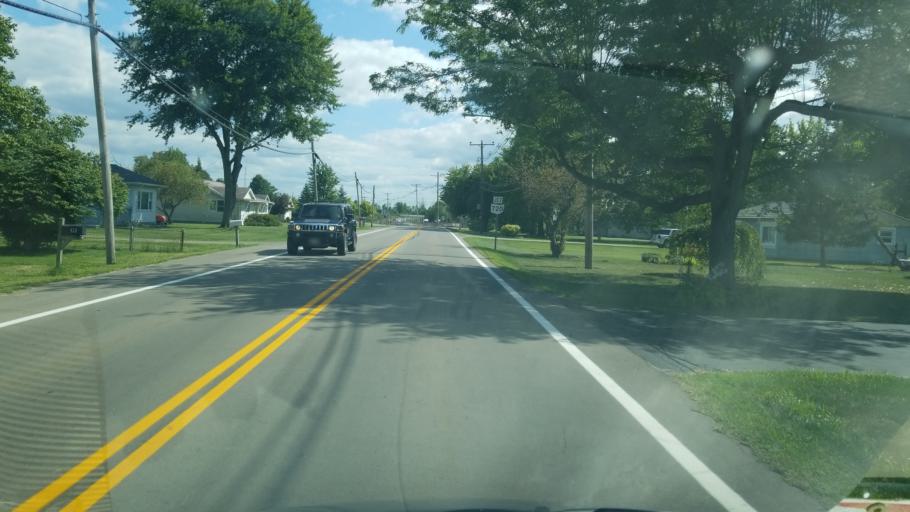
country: US
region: Ohio
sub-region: Logan County
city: Lakeview
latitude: 40.4792
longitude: -83.9236
